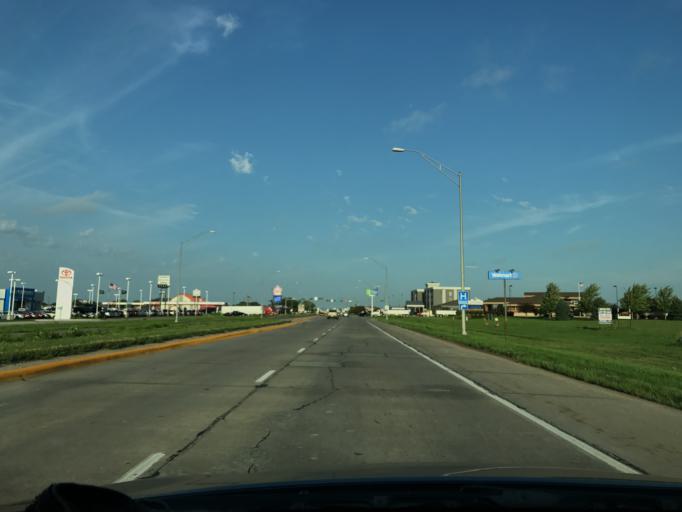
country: US
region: Nebraska
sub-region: Platte County
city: Columbus
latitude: 41.4386
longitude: -97.3169
